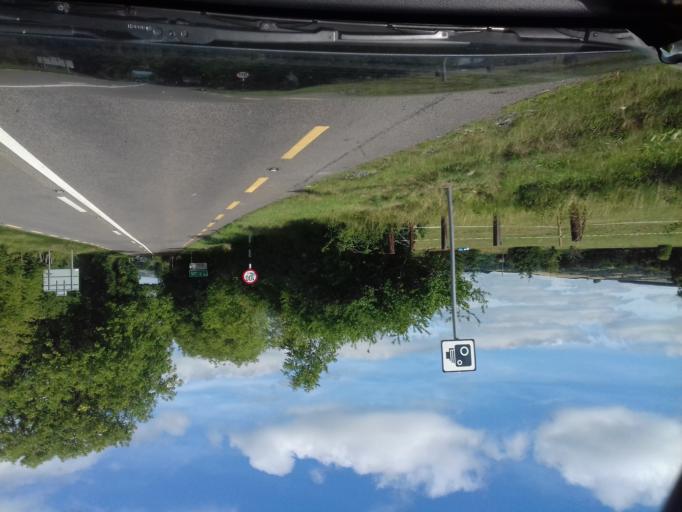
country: IE
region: Leinster
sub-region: Wicklow
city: Blessington
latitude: 53.1489
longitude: -6.5565
